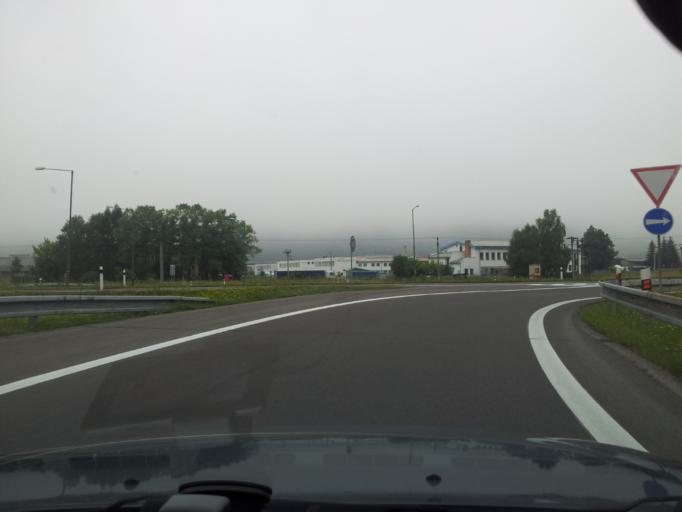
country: SK
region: Zilinsky
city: Cadca
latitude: 49.4021
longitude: 18.8432
